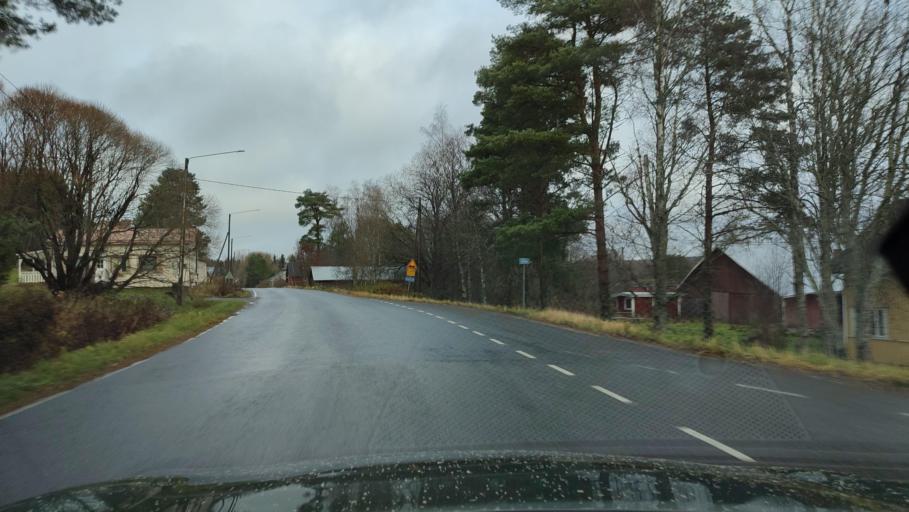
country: FI
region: Southern Ostrobothnia
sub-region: Suupohja
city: Karijoki
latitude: 62.3807
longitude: 21.5573
